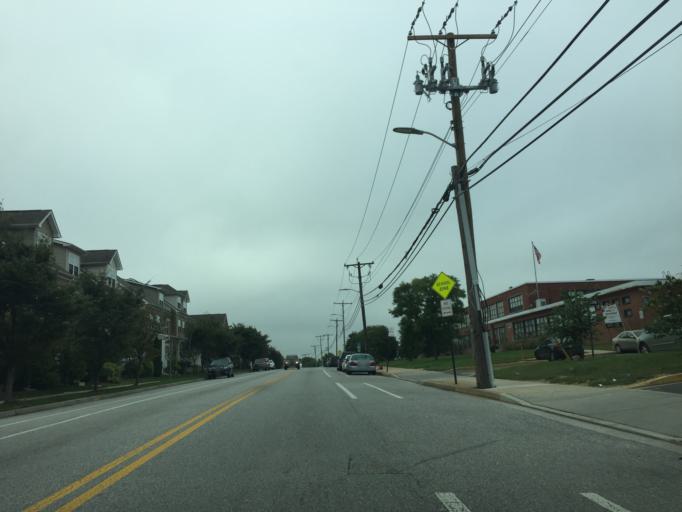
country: US
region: Maryland
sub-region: Baltimore County
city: Rosedale
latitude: 39.3207
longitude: -76.5404
